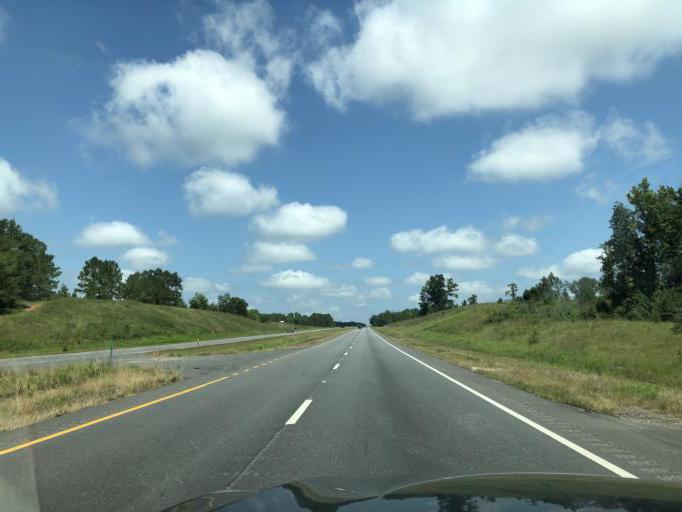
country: US
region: Alabama
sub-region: Henry County
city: Abbeville
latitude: 31.5195
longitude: -85.2910
